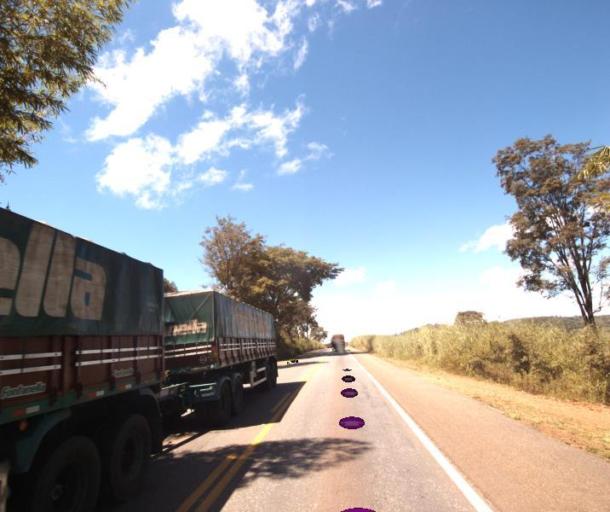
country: BR
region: Goias
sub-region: Pirenopolis
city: Pirenopolis
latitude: -16.0704
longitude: -49.0578
